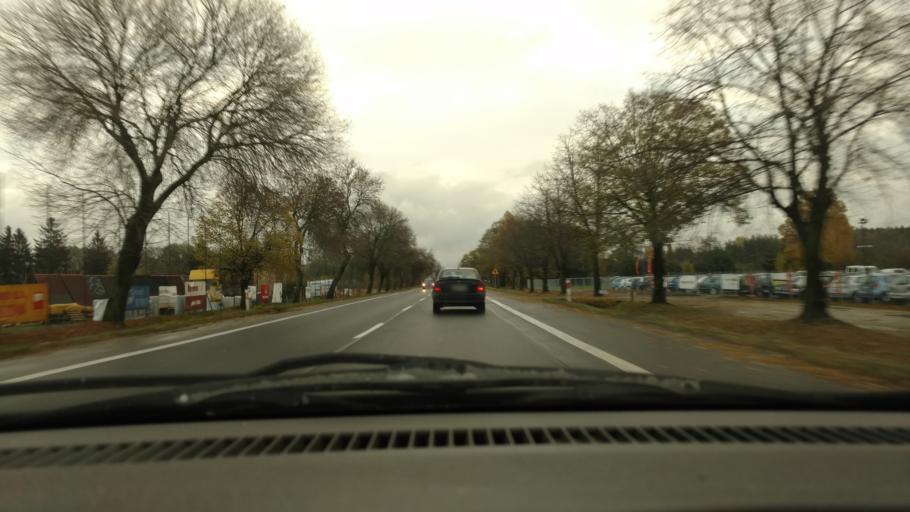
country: PL
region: Lodz Voivodeship
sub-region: Powiat zdunskowolski
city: Zdunska Wola
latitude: 51.5917
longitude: 19.0108
